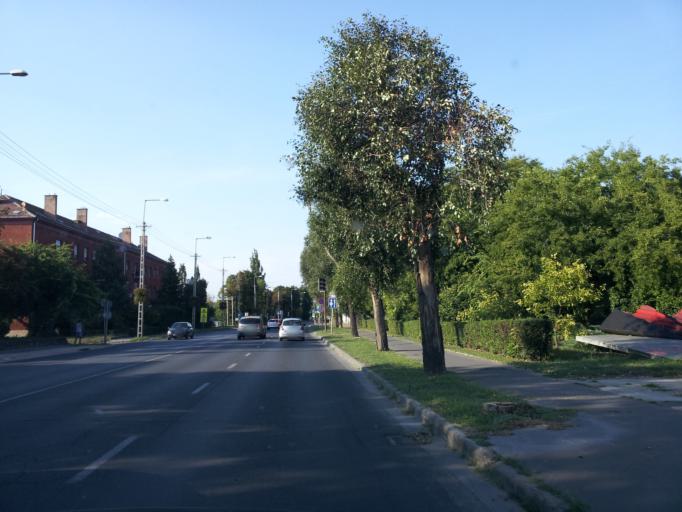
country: HU
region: Pest
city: Szentendre
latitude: 47.6557
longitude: 19.0729
